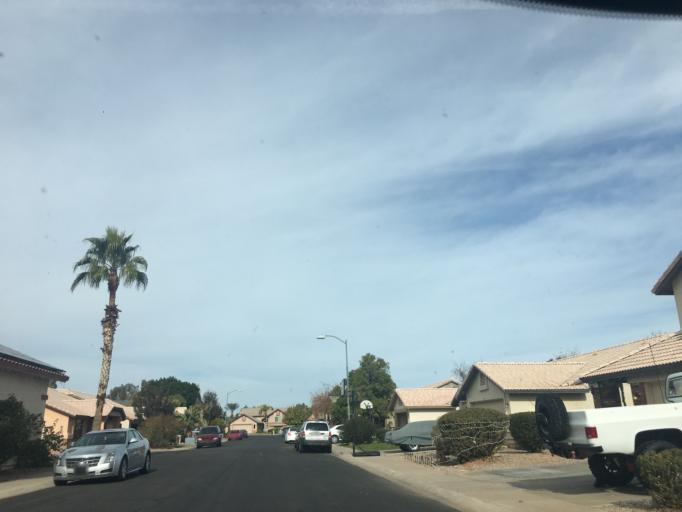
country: US
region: Arizona
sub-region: Maricopa County
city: Gilbert
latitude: 33.3481
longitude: -111.8009
